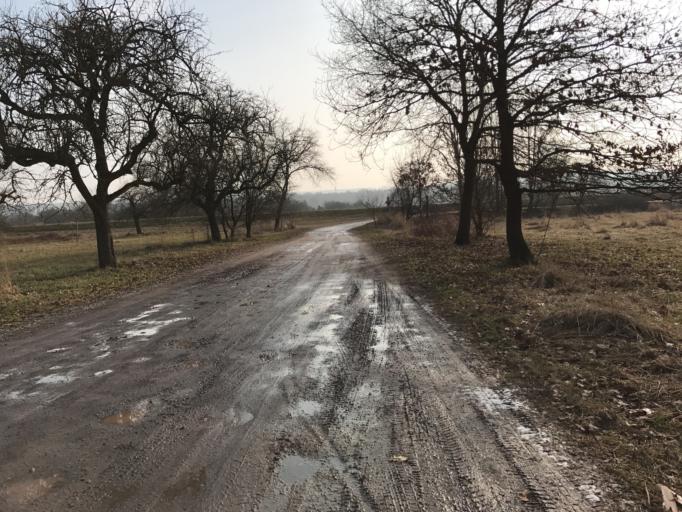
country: DE
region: Rheinland-Pfalz
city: Budenheim
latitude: 50.0224
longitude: 8.1481
